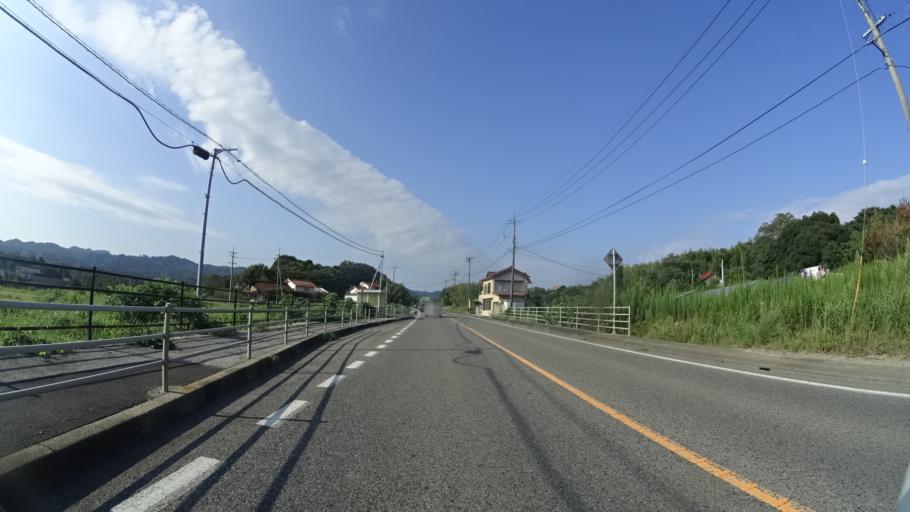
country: JP
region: Shimane
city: Izumo
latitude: 35.3055
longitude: 132.6547
